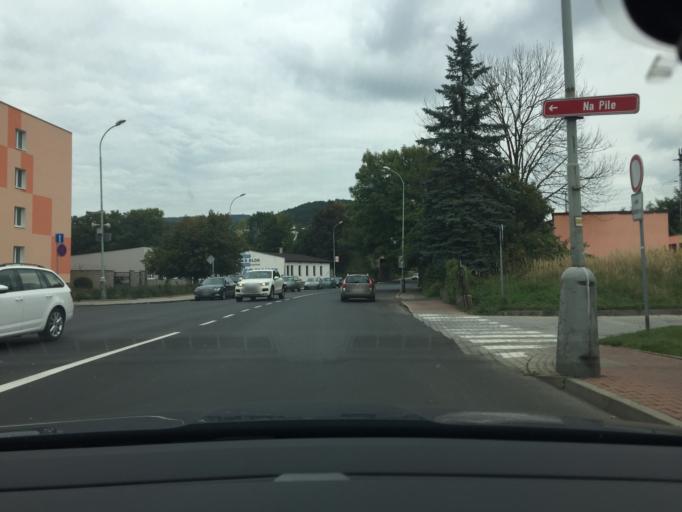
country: CZ
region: Ustecky
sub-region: Okres Usti nad Labem
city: Usti nad Labem
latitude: 50.6536
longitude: 14.0479
